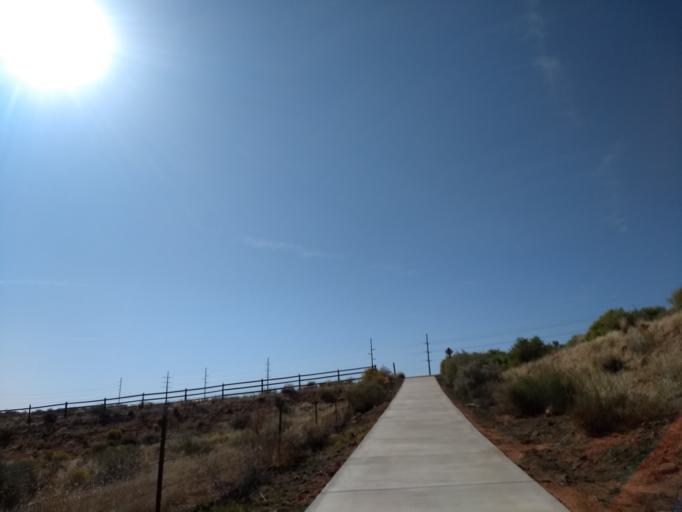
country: US
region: Utah
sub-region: Washington County
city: Saint George
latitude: 37.1269
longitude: -113.5826
